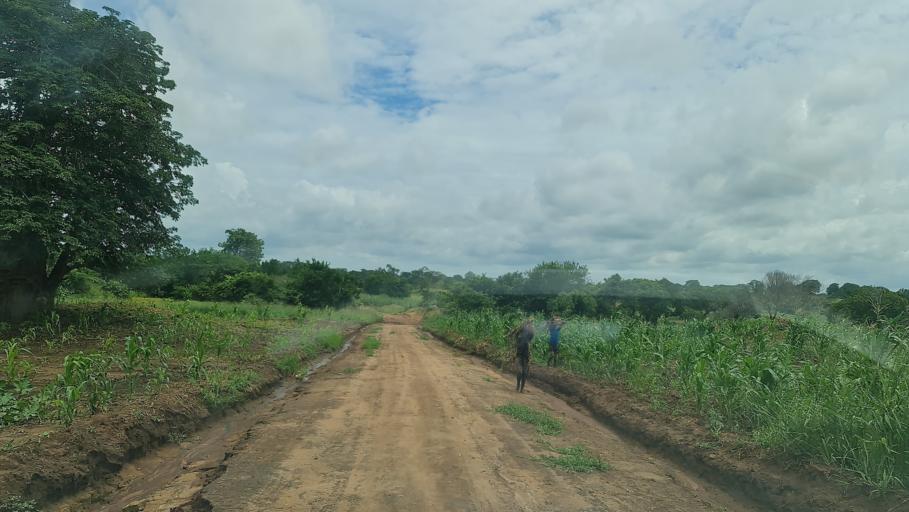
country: MZ
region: Cabo Delgado
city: Pemba
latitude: -13.5207
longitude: 40.0180
